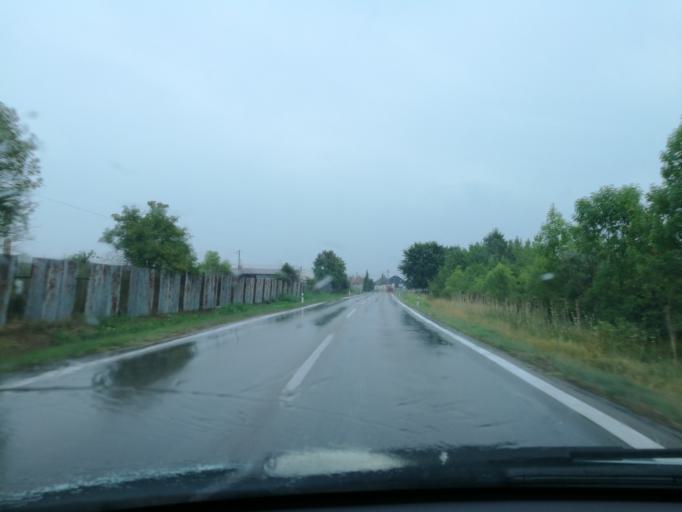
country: HU
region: Komarom-Esztergom
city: Almasfuzito
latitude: 47.7573
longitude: 18.2062
